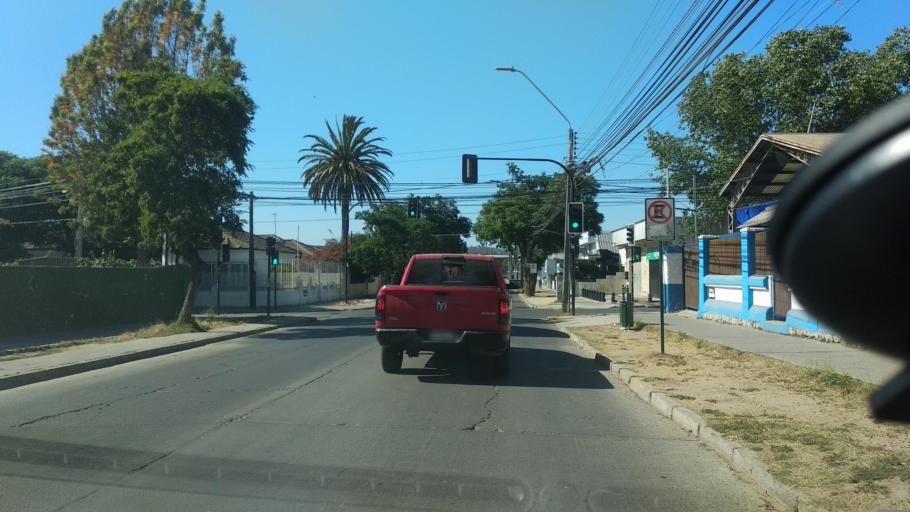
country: CL
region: Valparaiso
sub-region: Provincia de Marga Marga
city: Villa Alemana
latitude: -33.0469
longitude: -71.3742
